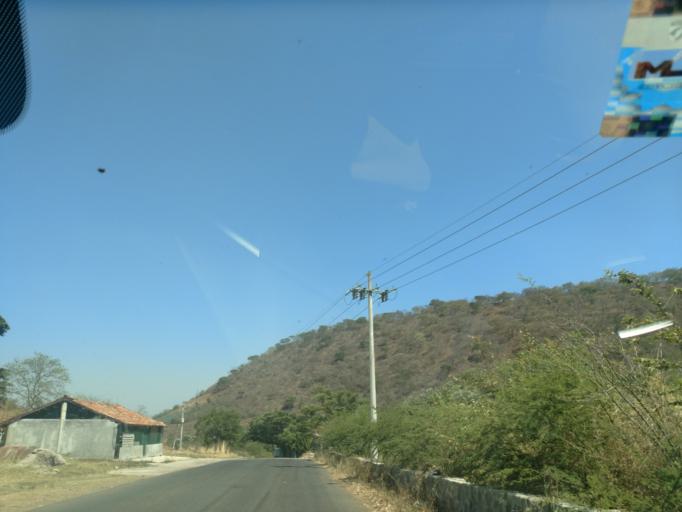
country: MX
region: Nayarit
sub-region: Tepic
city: La Corregidora
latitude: 21.4747
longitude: -104.6702
